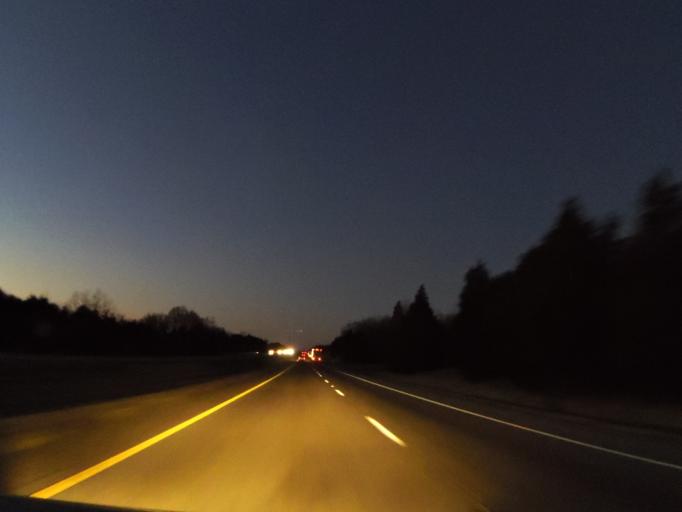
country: US
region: Tennessee
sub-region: Cocke County
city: Newport
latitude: 35.9980
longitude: -83.2876
